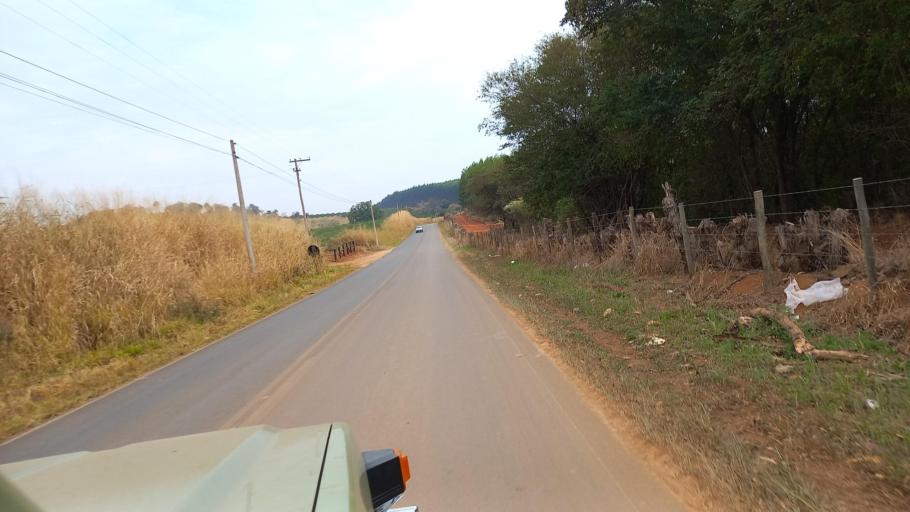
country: BR
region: Sao Paulo
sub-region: Moji-Guacu
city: Mogi-Gaucu
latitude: -22.3297
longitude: -46.8613
